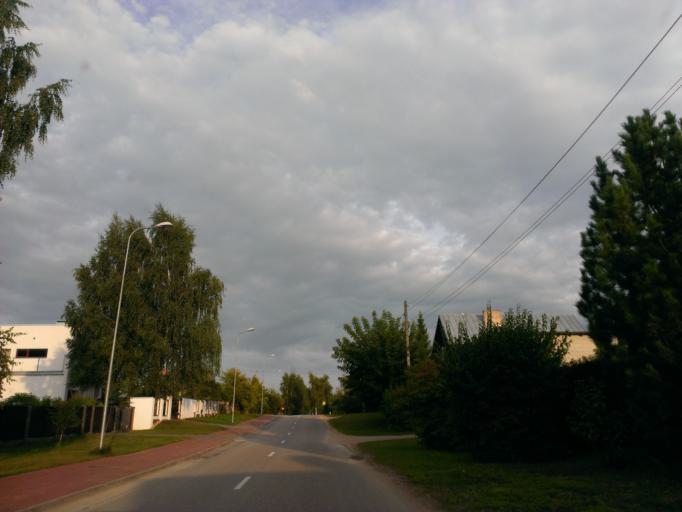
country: LV
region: Ikskile
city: Ikskile
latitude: 56.8357
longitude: 24.5131
